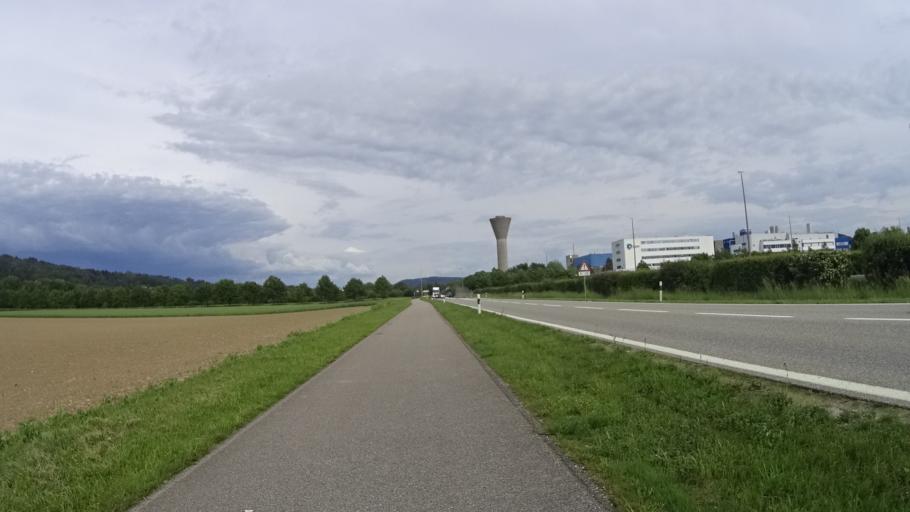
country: CH
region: Aargau
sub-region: Bezirk Laufenburg
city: Eiken
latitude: 47.5518
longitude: 7.9766
